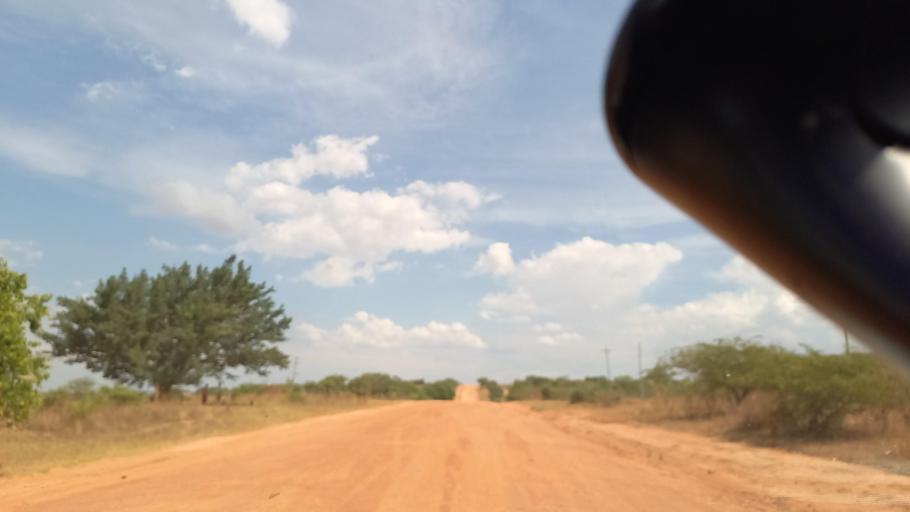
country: ZM
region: Lusaka
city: Kafue
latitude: -16.1259
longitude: 28.0439
